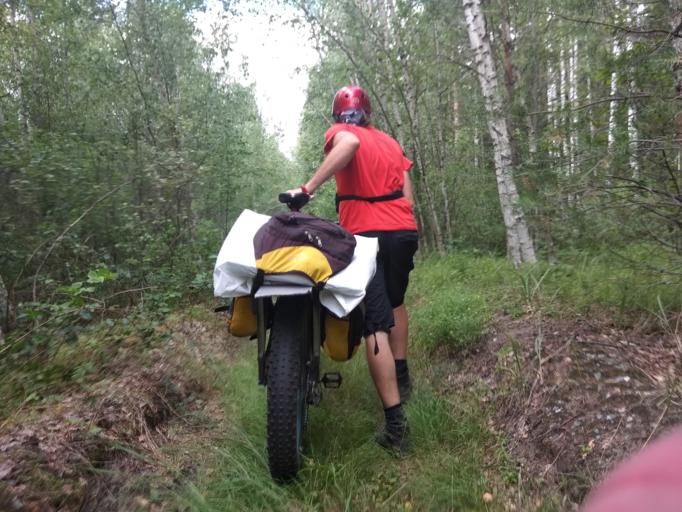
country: RU
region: Moskovskaya
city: Misheronskiy
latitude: 55.6458
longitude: 39.6953
